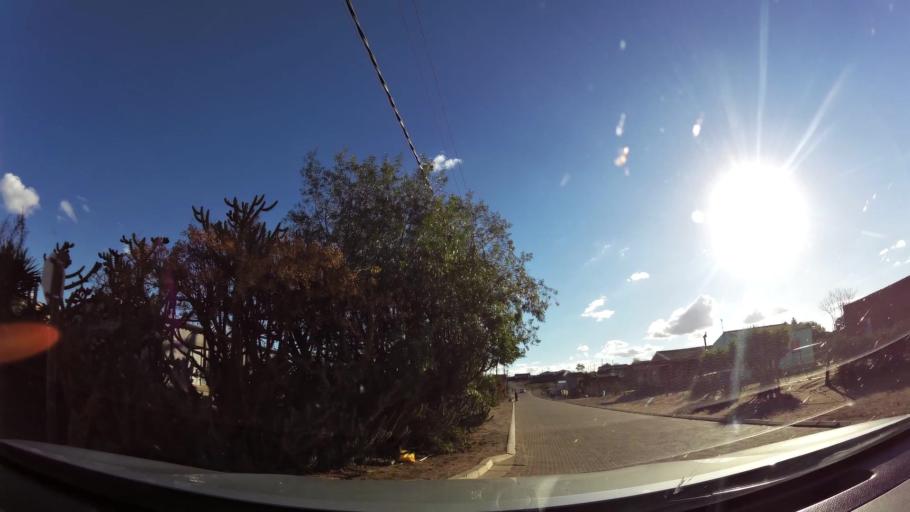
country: ZA
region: Western Cape
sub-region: Eden District Municipality
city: Riversdale
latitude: -34.1064
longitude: 20.9691
